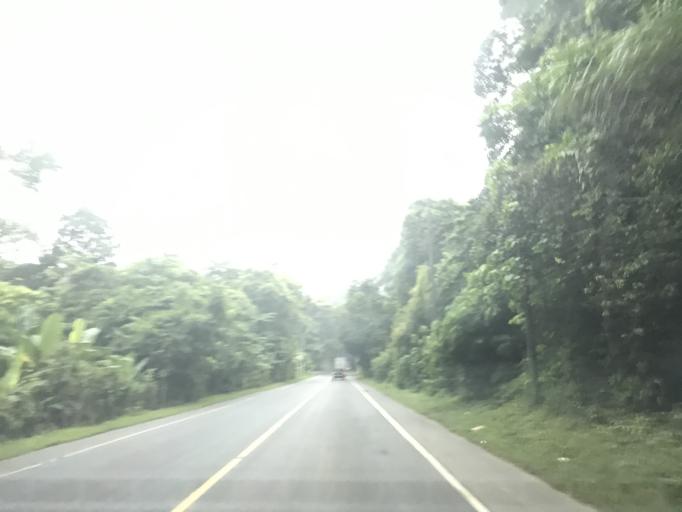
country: GT
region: Izabal
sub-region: Municipio de Puerto Barrios
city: Puerto Barrios
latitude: 15.6657
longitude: -88.5592
